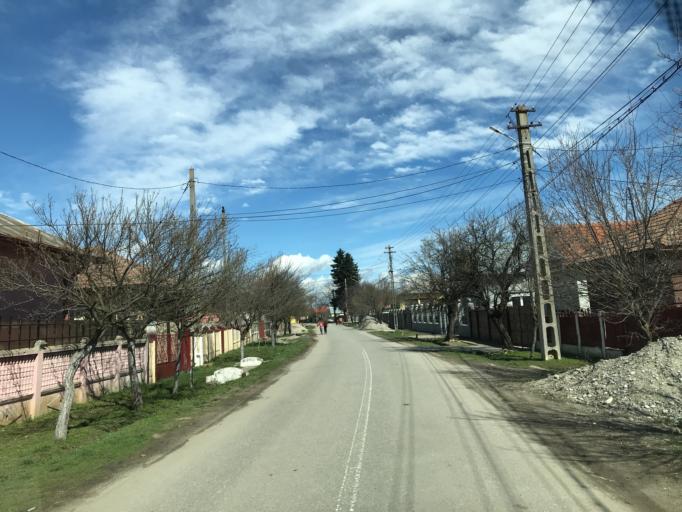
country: RO
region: Olt
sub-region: Comuna Osica de Sus
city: Osica de Sus
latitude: 44.2531
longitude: 24.3152
